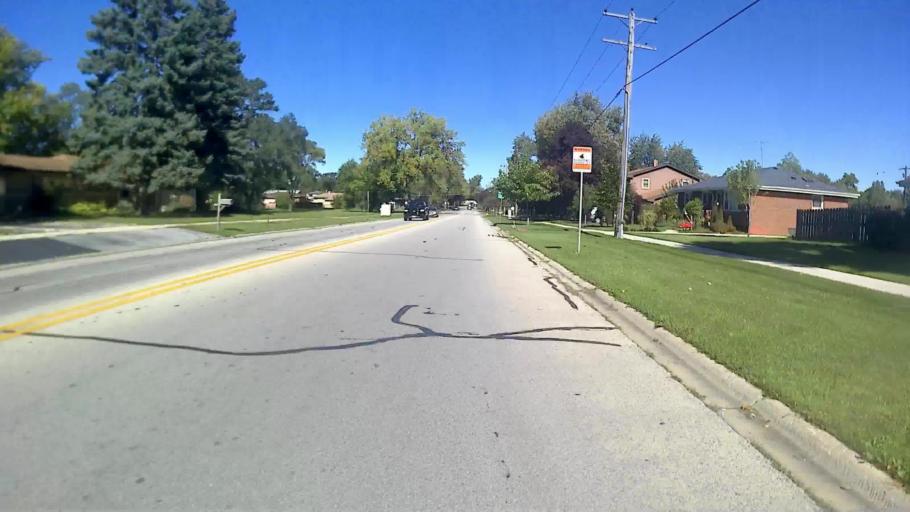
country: US
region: Illinois
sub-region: DuPage County
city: Addison
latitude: 41.9418
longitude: -88.0033
